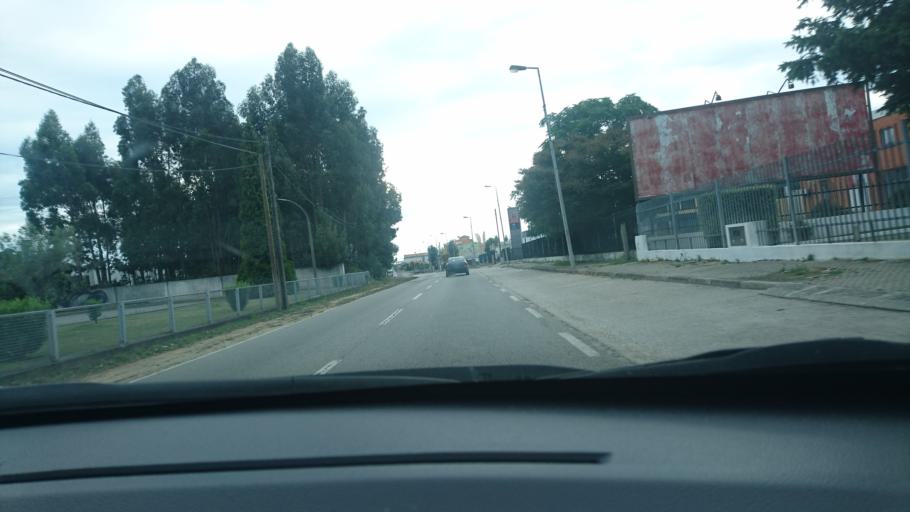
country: PT
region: Aveiro
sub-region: Santa Maria da Feira
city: Rio Meao
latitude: 40.9600
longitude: -8.5959
